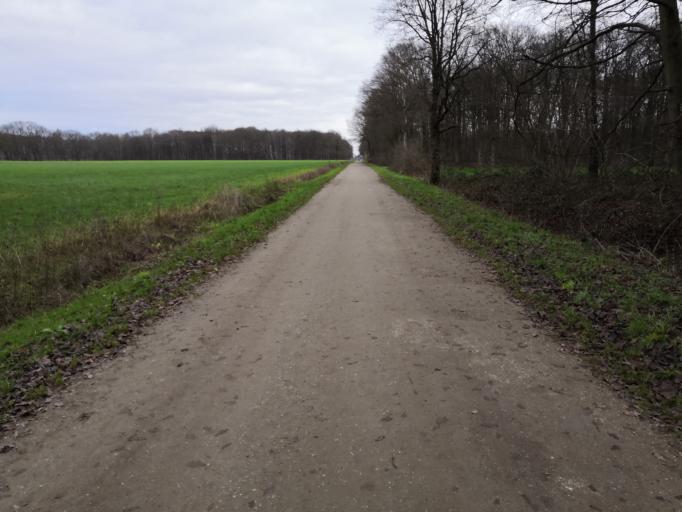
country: DE
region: North Rhine-Westphalia
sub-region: Regierungsbezirk Dusseldorf
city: Wachtendonk
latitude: 51.4365
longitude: 6.3713
